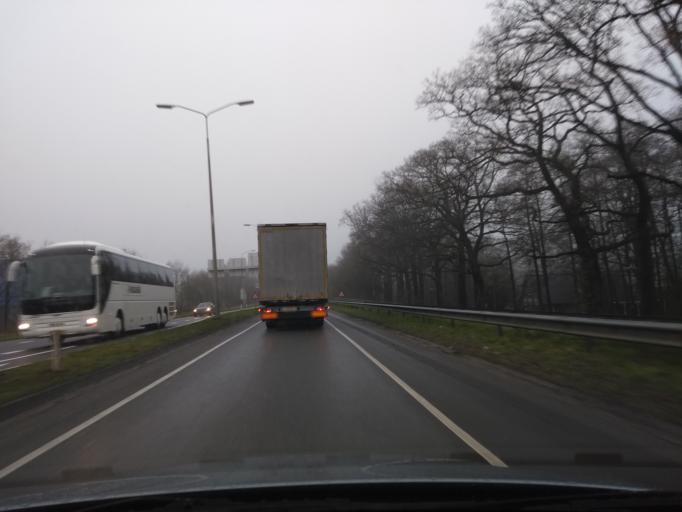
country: NL
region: Overijssel
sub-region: Gemeente Wierden
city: Wierden
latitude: 52.3560
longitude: 6.6232
